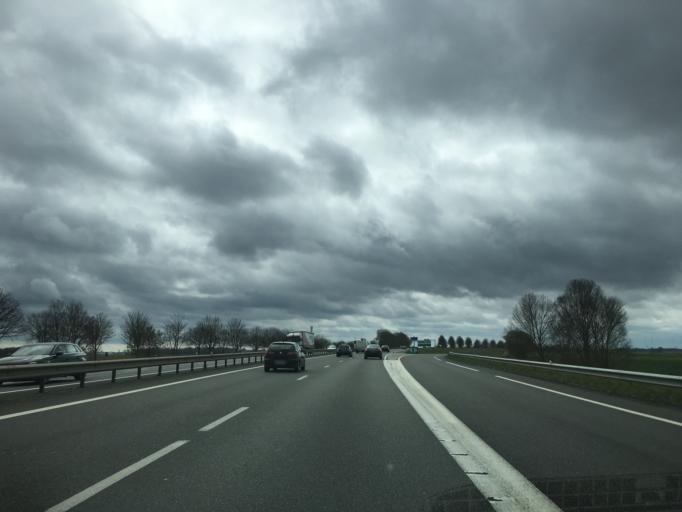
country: FR
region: Ile-de-France
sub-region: Departement de Seine-et-Marne
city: Moissy-Cramayel
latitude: 48.6369
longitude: 2.6285
